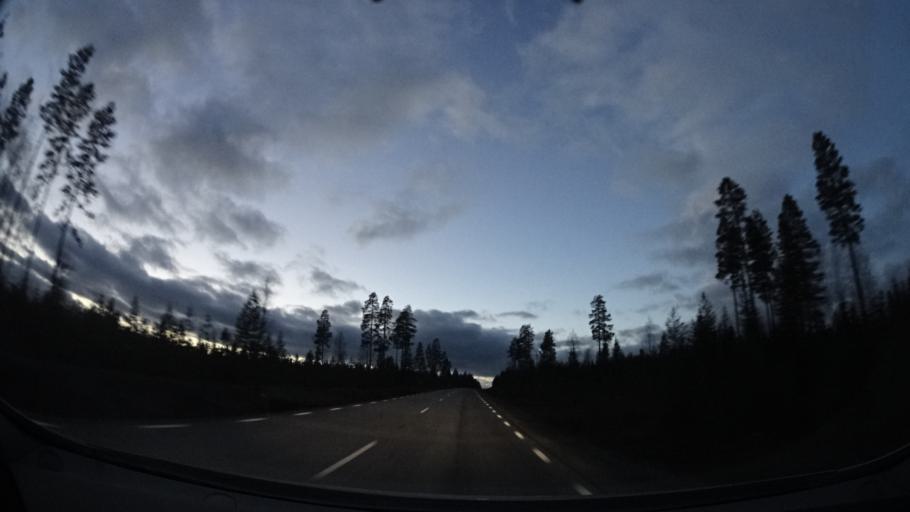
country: SE
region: Vaesterbotten
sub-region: Dorotea Kommun
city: Dorotea
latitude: 64.2220
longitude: 16.8636
